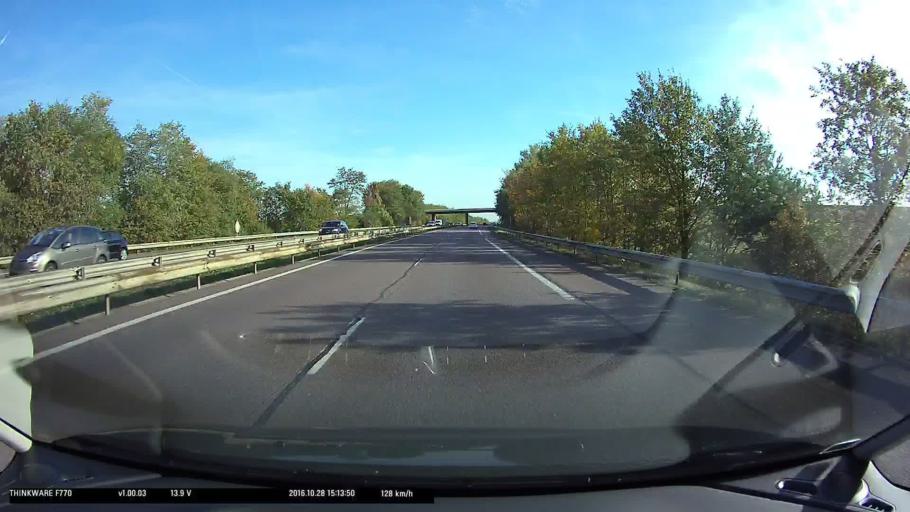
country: FR
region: Alsace
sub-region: Departement du Bas-Rhin
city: Mommenheim
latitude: 48.7613
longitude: 7.6642
